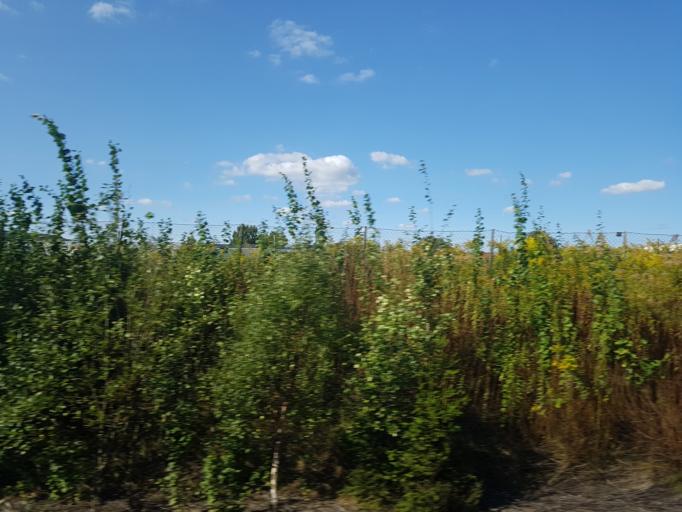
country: NO
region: Buskerud
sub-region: Lier
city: Lierbyen
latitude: 59.7546
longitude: 10.2670
